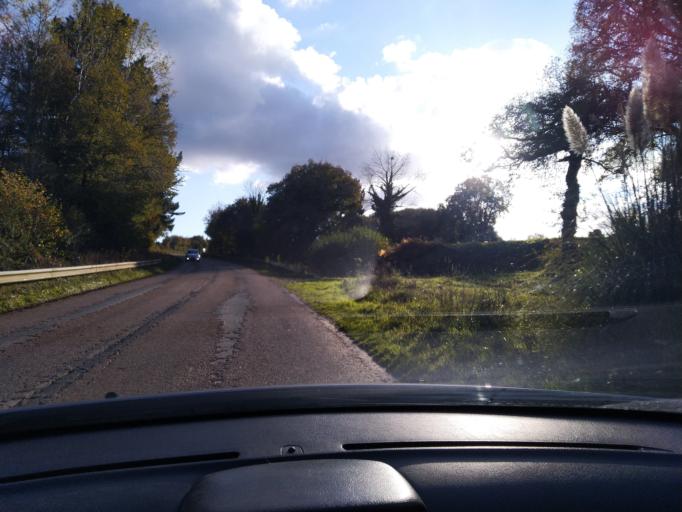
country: FR
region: Brittany
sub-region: Departement du Finistere
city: Guerlesquin
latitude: 48.5865
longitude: -3.6071
